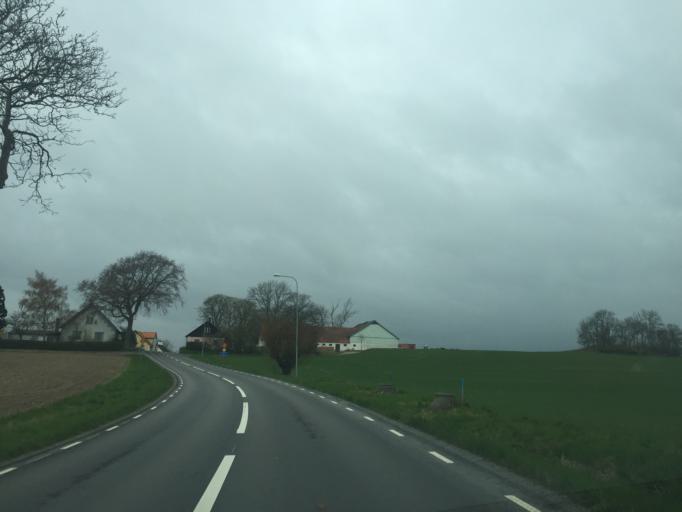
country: SE
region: Skane
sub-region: Skurups Kommun
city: Skivarp
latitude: 55.4232
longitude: 13.6203
